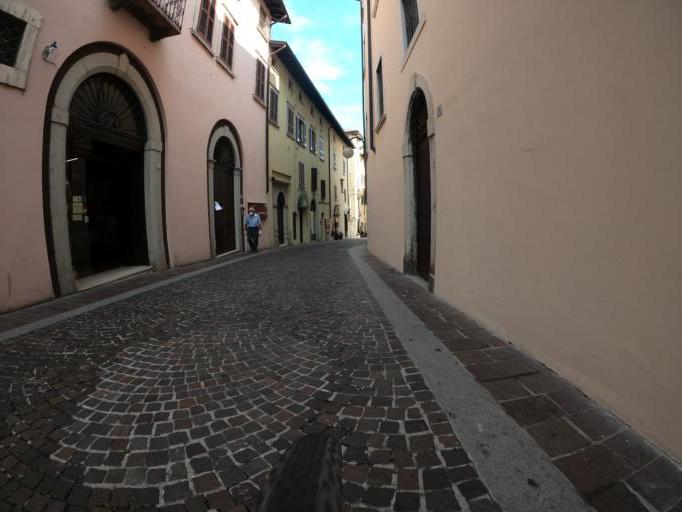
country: IT
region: Lombardy
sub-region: Provincia di Brescia
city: Desenzano del Garda
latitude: 45.4695
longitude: 10.5392
